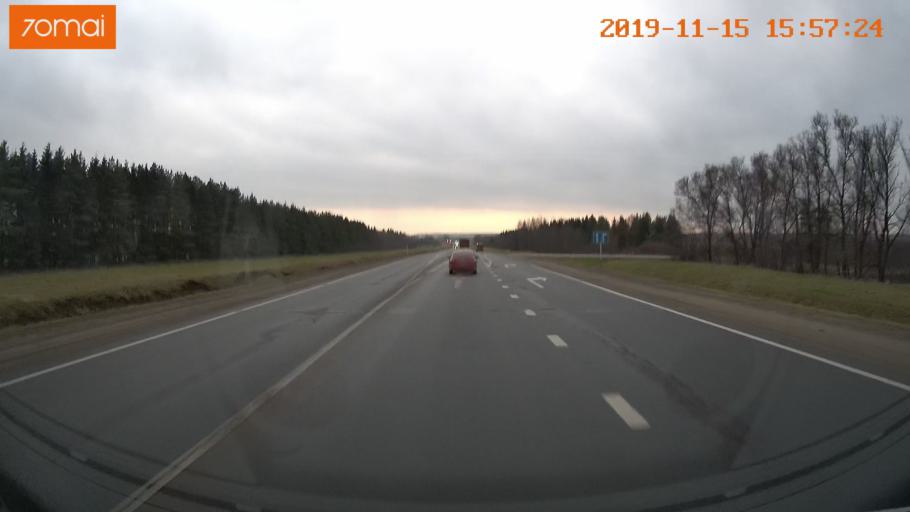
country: RU
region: Jaroslavl
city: Yaroslavl
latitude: 57.8306
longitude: 39.9639
